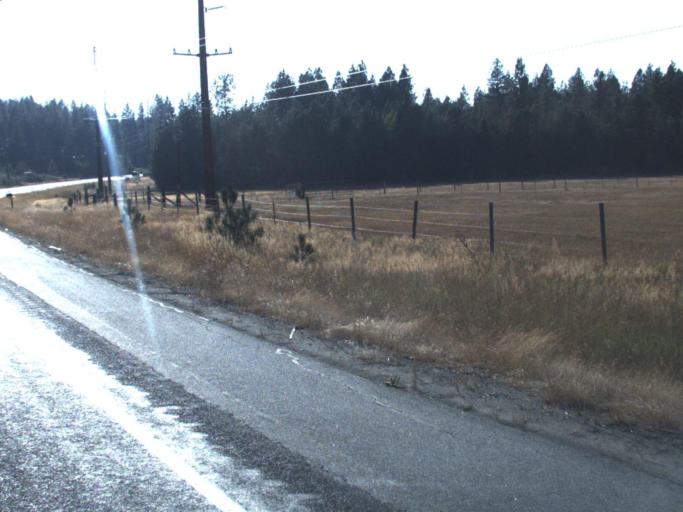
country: US
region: Washington
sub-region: Pend Oreille County
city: Newport
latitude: 48.0985
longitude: -117.2539
